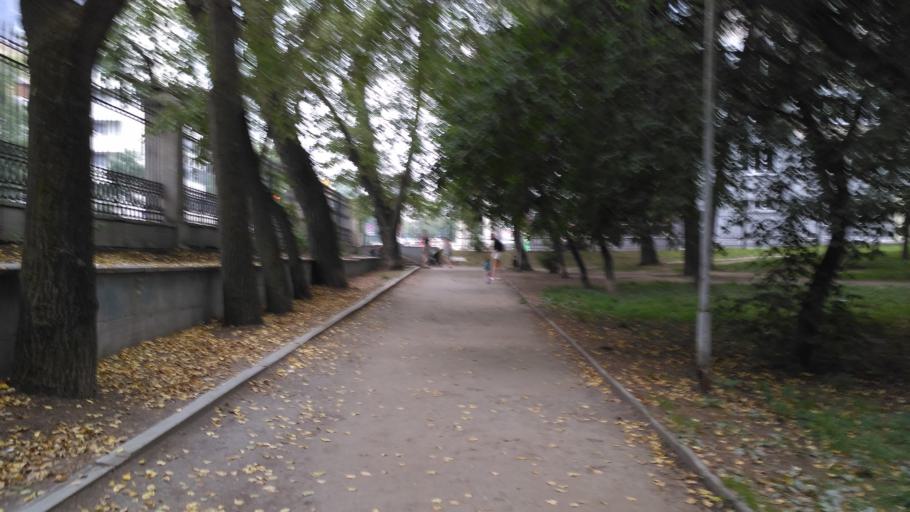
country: RU
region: Sverdlovsk
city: Yekaterinburg
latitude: 56.8458
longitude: 60.6154
